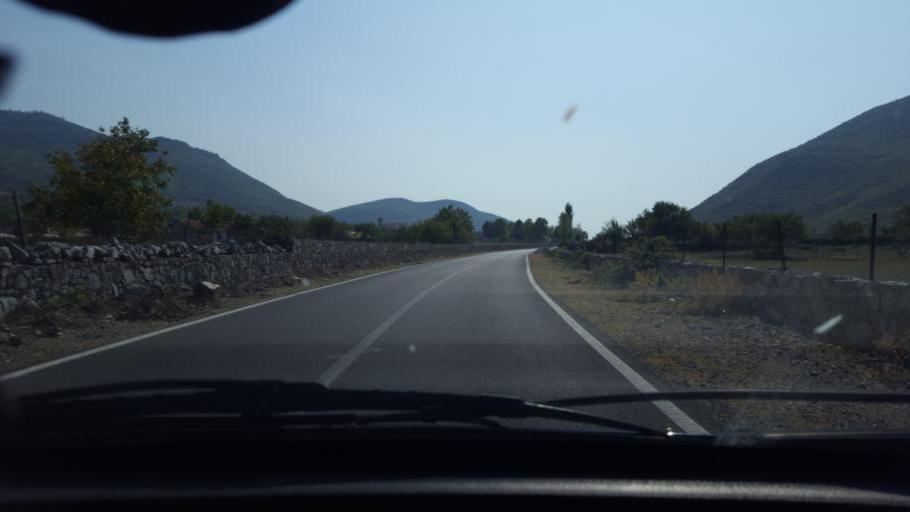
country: AL
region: Shkoder
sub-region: Rrethi i Malesia e Madhe
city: Kastrat
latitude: 42.4029
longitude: 19.4960
